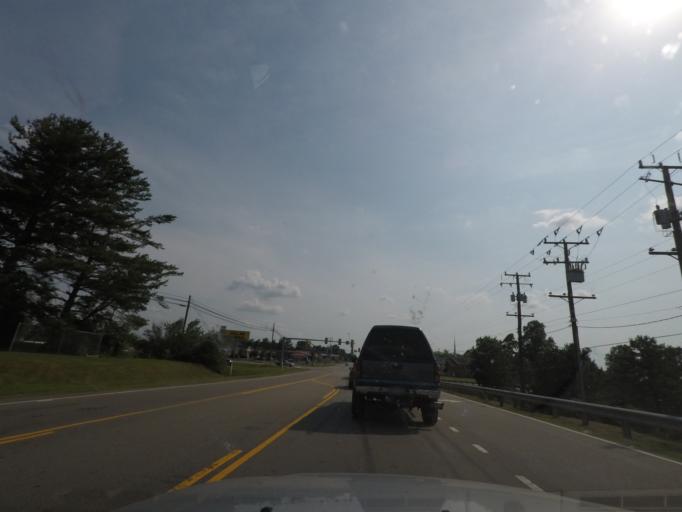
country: US
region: Virginia
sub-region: Buckingham County
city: Buckingham
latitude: 37.5442
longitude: -78.4734
